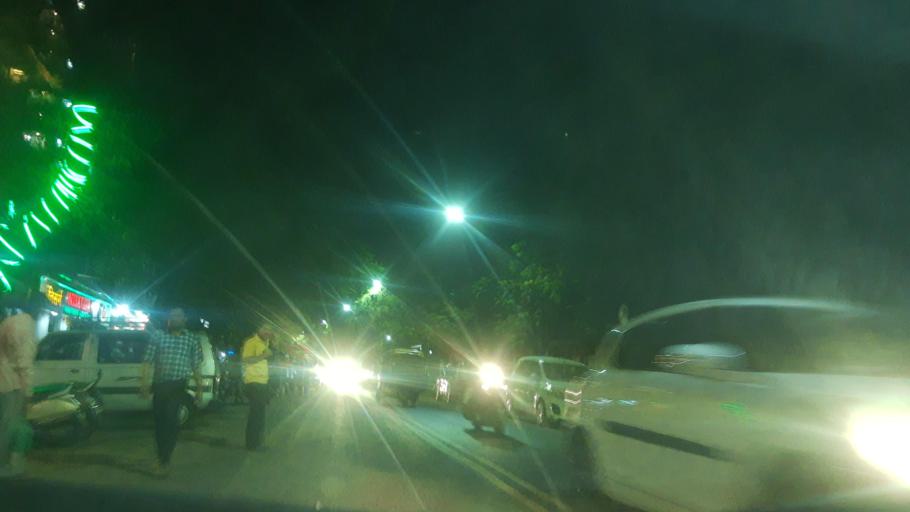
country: IN
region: Maharashtra
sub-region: Thane
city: Thane
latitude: 19.1989
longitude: 72.9636
